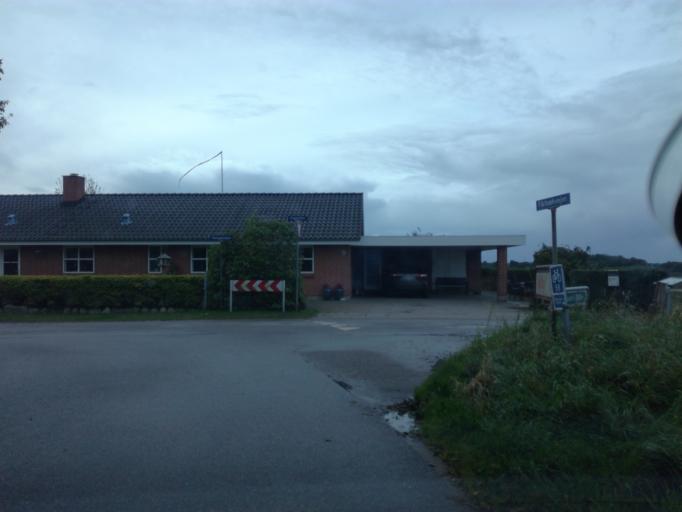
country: DK
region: South Denmark
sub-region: Fredericia Kommune
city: Fredericia
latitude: 55.5967
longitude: 9.7079
